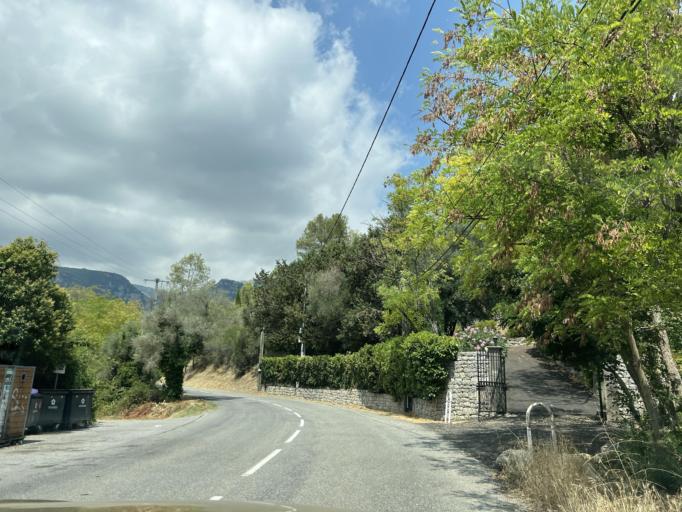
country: FR
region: Provence-Alpes-Cote d'Azur
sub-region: Departement des Alpes-Maritimes
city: Le Rouret
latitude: 43.6997
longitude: 7.0078
